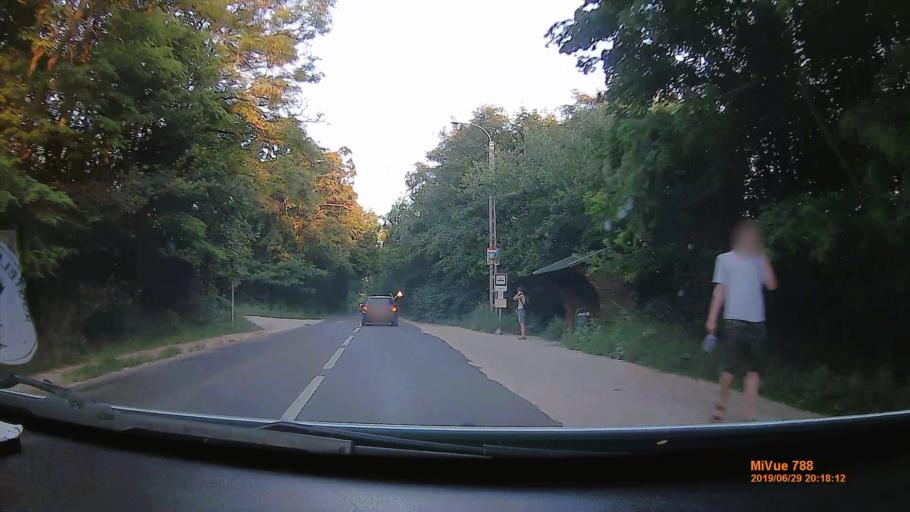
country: HU
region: Pest
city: Paty
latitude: 47.5067
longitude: 18.8545
